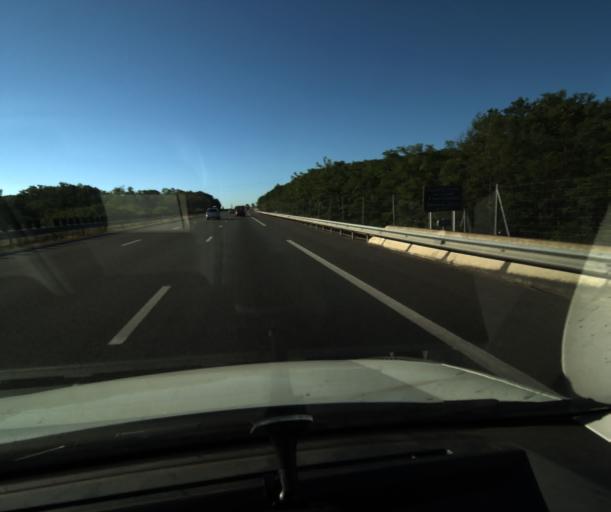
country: FR
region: Midi-Pyrenees
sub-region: Departement de la Haute-Garonne
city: Castelnau-d'Estretefonds
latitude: 43.8057
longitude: 1.3667
